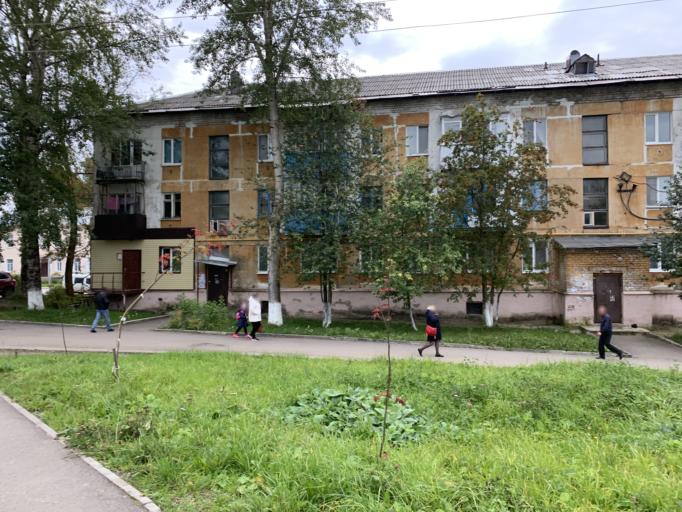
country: RU
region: Perm
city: Gubakha
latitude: 58.8394
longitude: 57.5538
